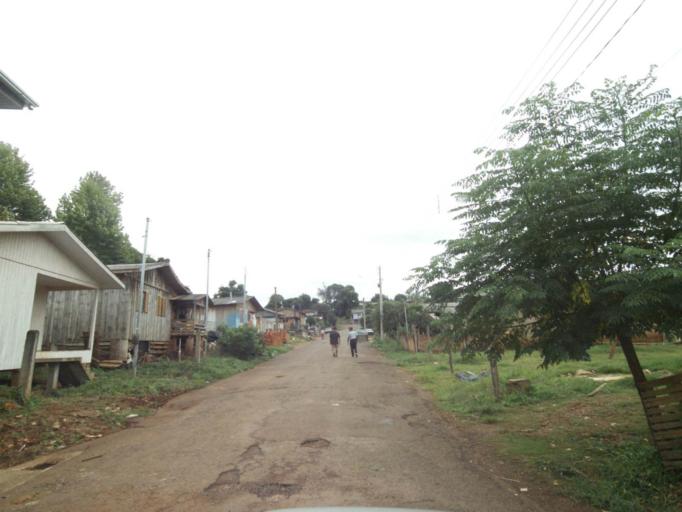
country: BR
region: Rio Grande do Sul
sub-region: Lagoa Vermelha
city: Lagoa Vermelha
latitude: -28.2156
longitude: -51.5380
